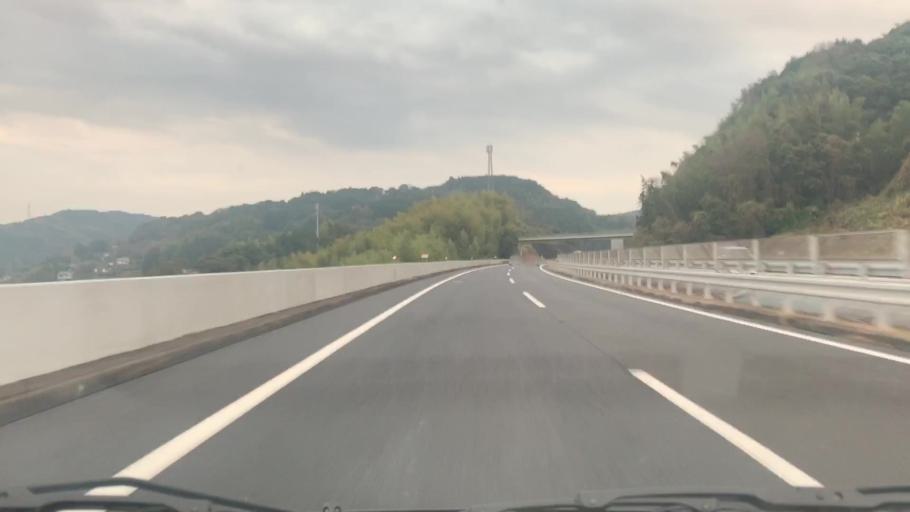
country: JP
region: Nagasaki
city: Omura
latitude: 32.8874
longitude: 129.9933
